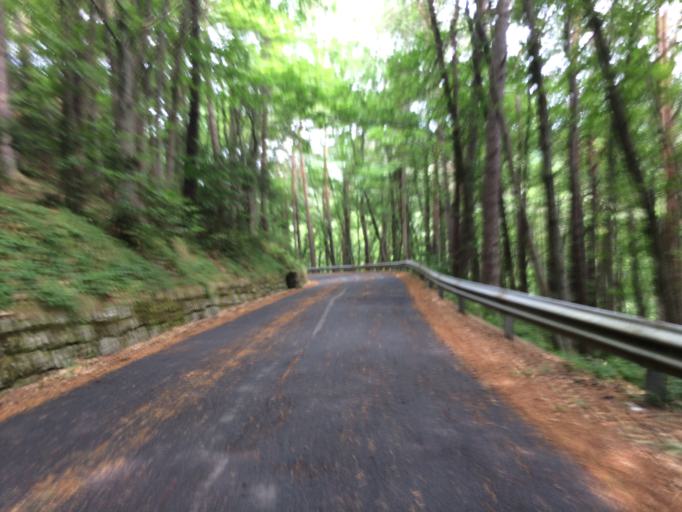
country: IT
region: Liguria
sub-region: Provincia di Imperia
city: Bajardo
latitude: 43.8986
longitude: 7.7285
